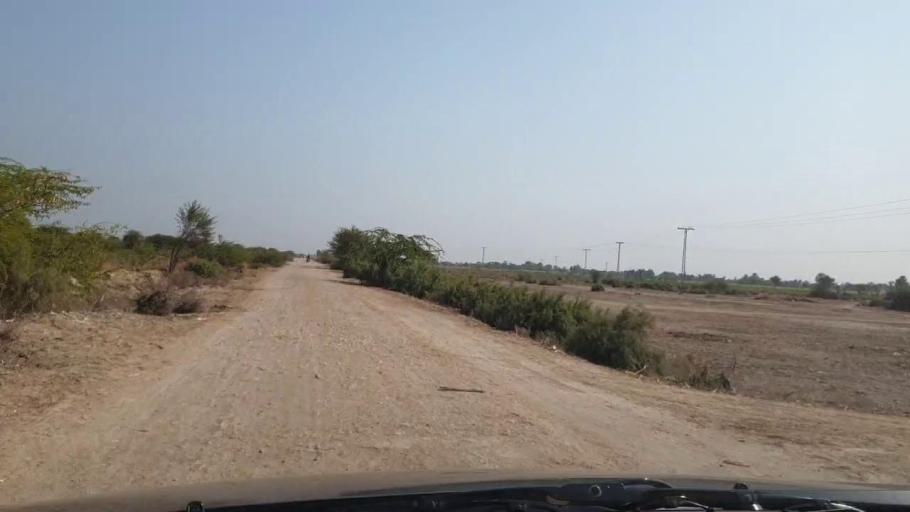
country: PK
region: Sindh
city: Jhol
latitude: 25.9966
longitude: 68.9187
